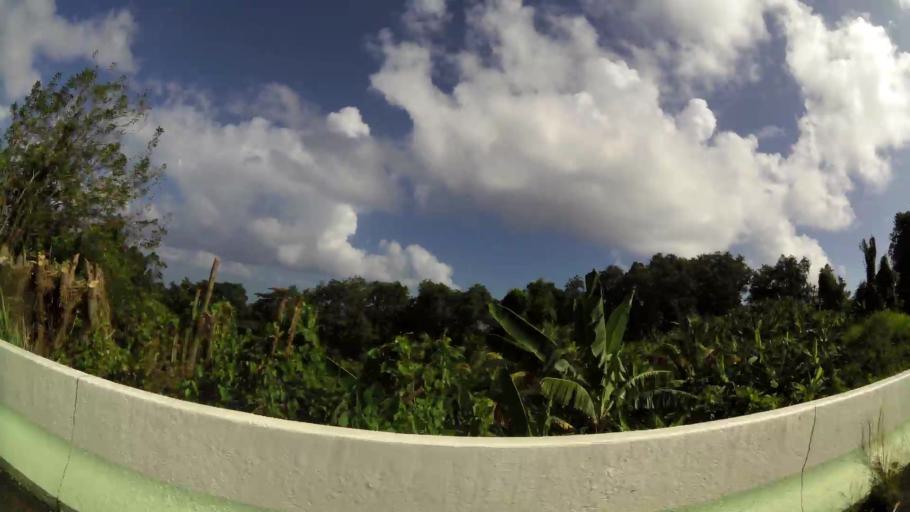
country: MQ
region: Martinique
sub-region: Martinique
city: Sainte-Marie
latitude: 14.8058
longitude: -61.0151
